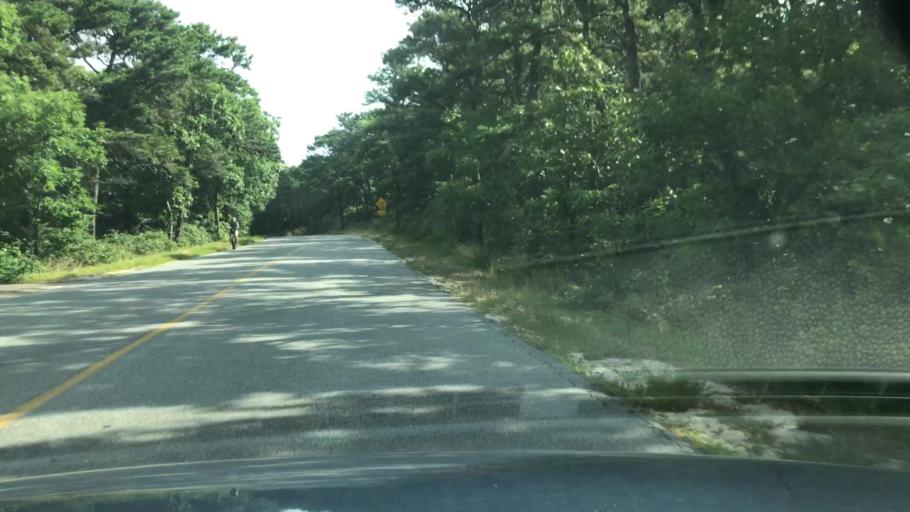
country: US
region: Massachusetts
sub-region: Barnstable County
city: Truro
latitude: 42.0303
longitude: -70.0676
